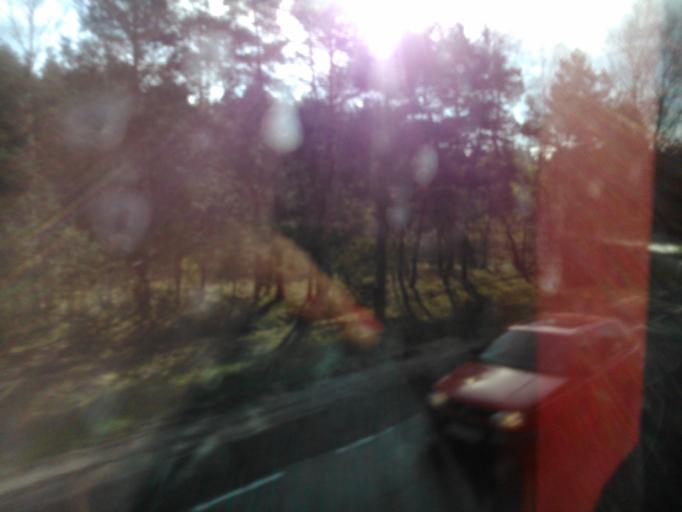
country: PL
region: Kujawsko-Pomorskie
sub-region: Torun
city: Torun
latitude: 52.9782
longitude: 18.6740
